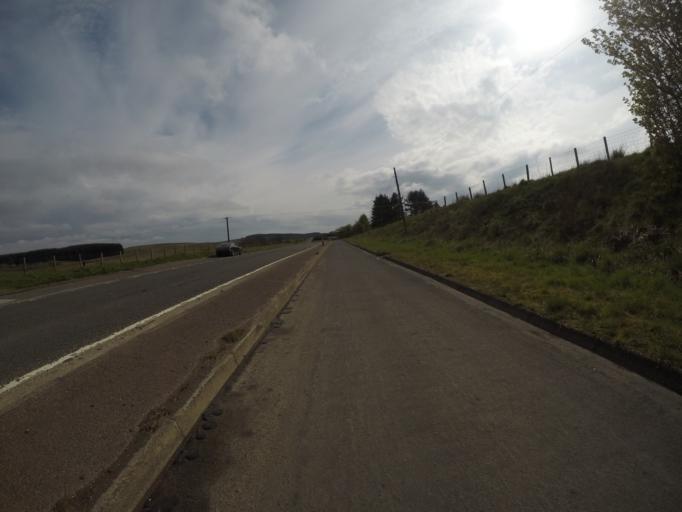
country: GB
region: Scotland
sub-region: East Renfrewshire
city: Newton Mearns
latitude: 55.7366
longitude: -4.3793
